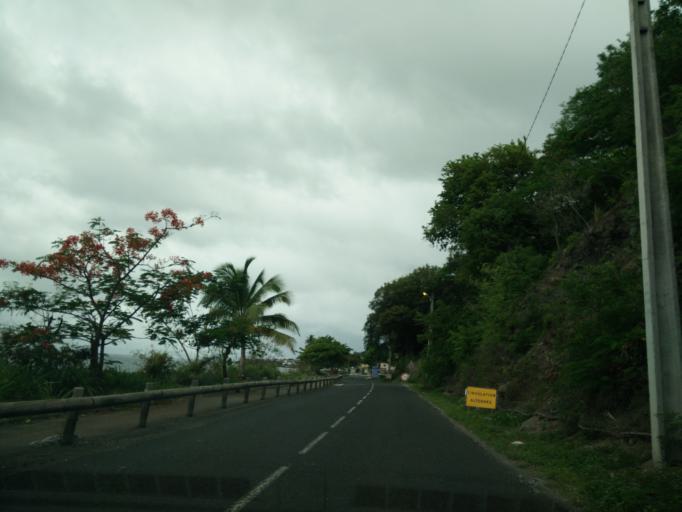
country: MQ
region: Martinique
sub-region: Martinique
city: Saint-Pierre
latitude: 14.7903
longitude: -61.2194
